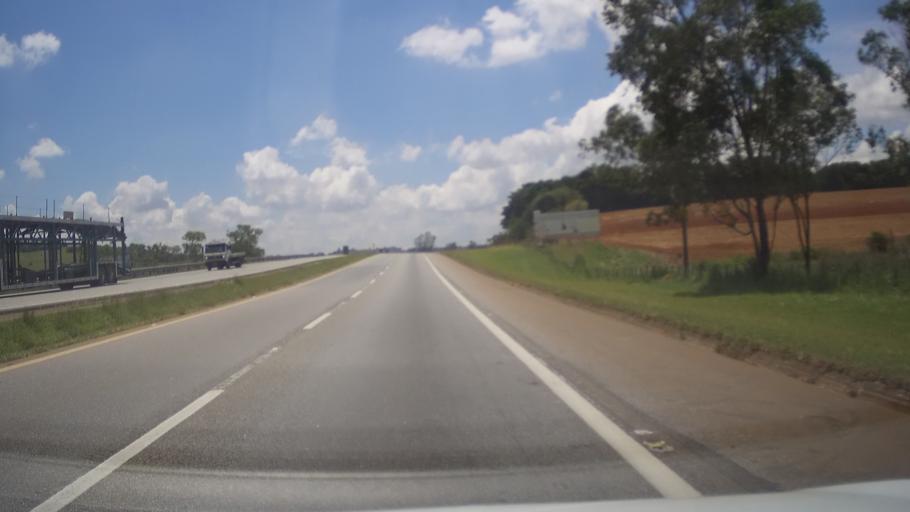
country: BR
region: Minas Gerais
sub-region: Sao Goncalo Do Sapucai
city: Sao Goncalo do Sapucai
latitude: -21.9180
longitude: -45.5925
